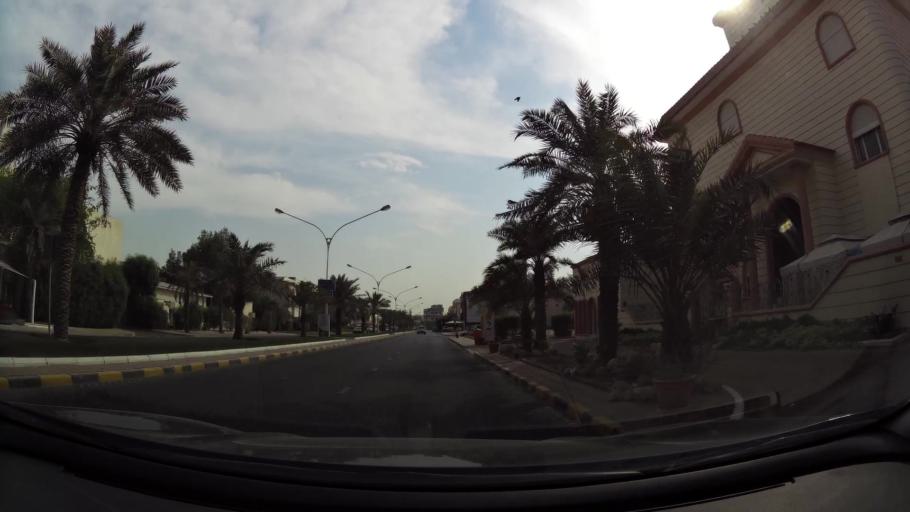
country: KW
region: Al Asimah
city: Ash Shamiyah
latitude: 29.3169
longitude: 47.9680
